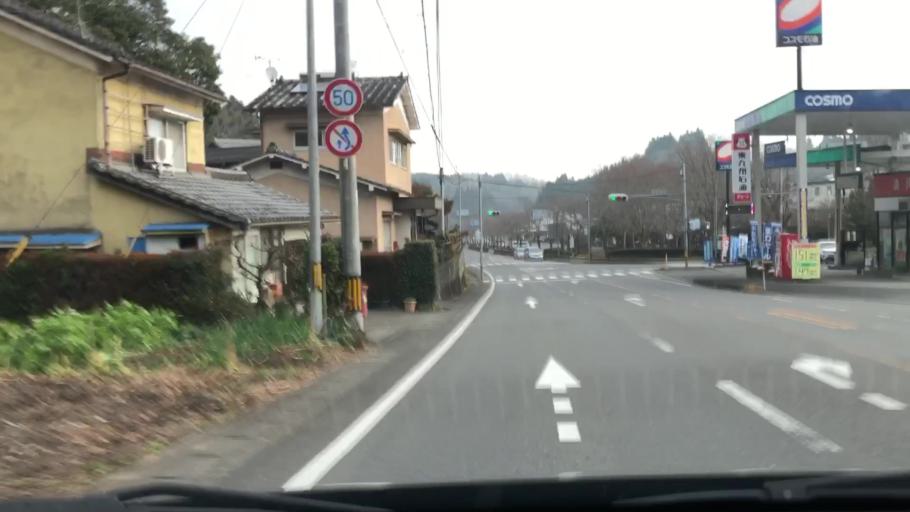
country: JP
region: Oita
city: Takedamachi
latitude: 32.9707
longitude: 131.5157
